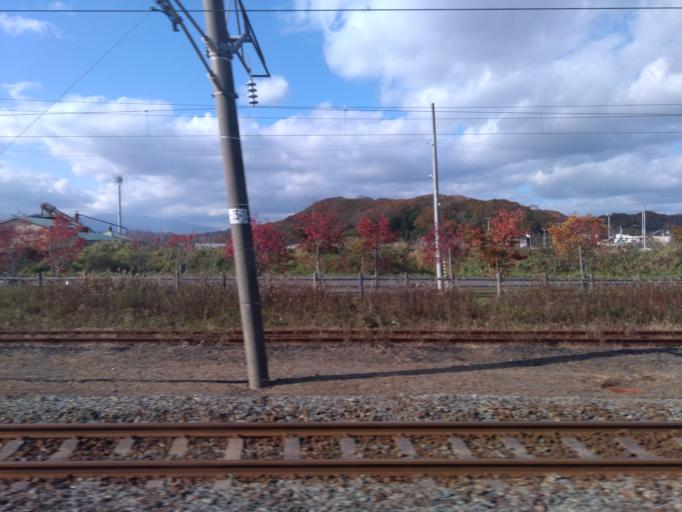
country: JP
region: Hokkaido
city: Shiraoi
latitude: 42.5555
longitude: 141.3609
